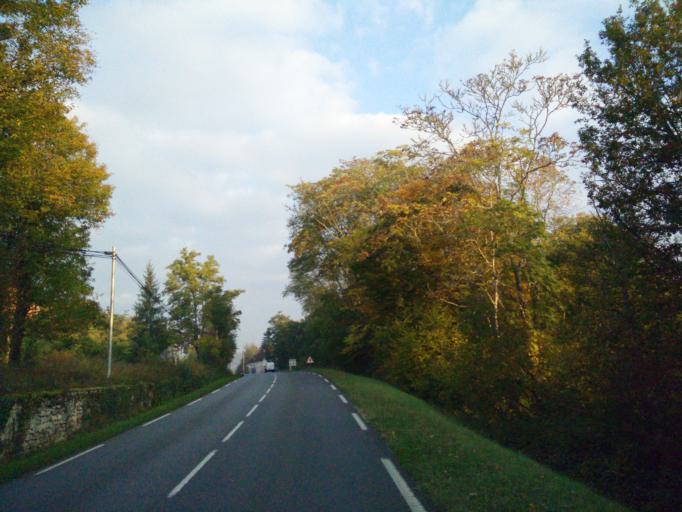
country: FR
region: Aquitaine
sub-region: Departement de la Dordogne
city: Le Bugue
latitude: 44.9763
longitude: 0.9580
